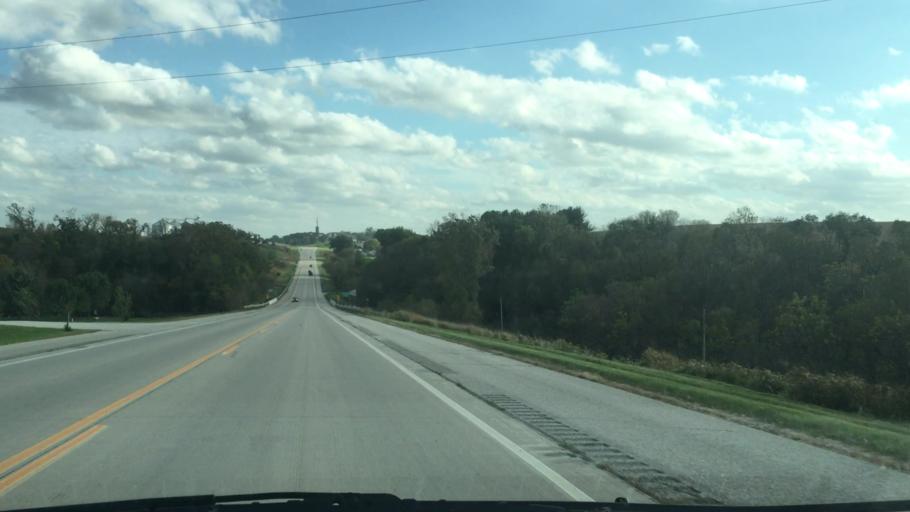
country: US
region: Minnesota
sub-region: Fillmore County
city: Preston
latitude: 43.6997
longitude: -92.1025
